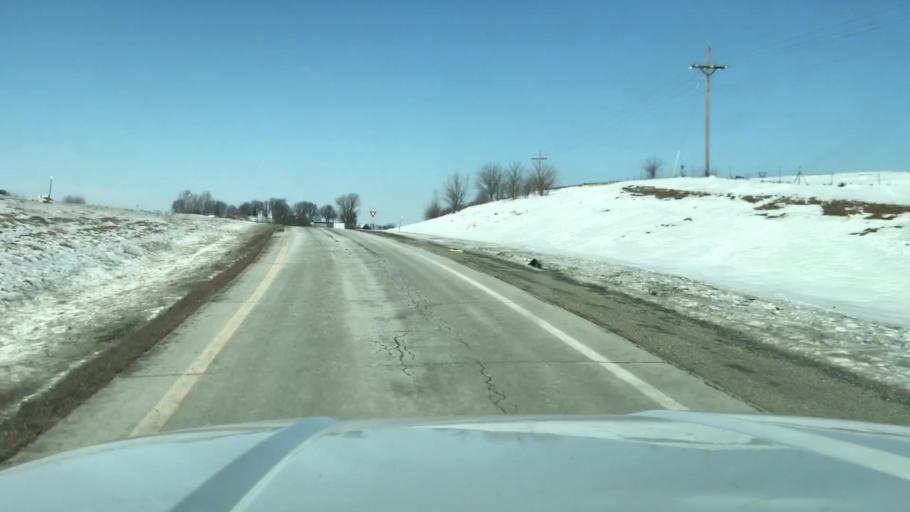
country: US
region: Missouri
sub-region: Andrew County
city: Savannah
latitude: 39.9632
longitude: -94.8622
